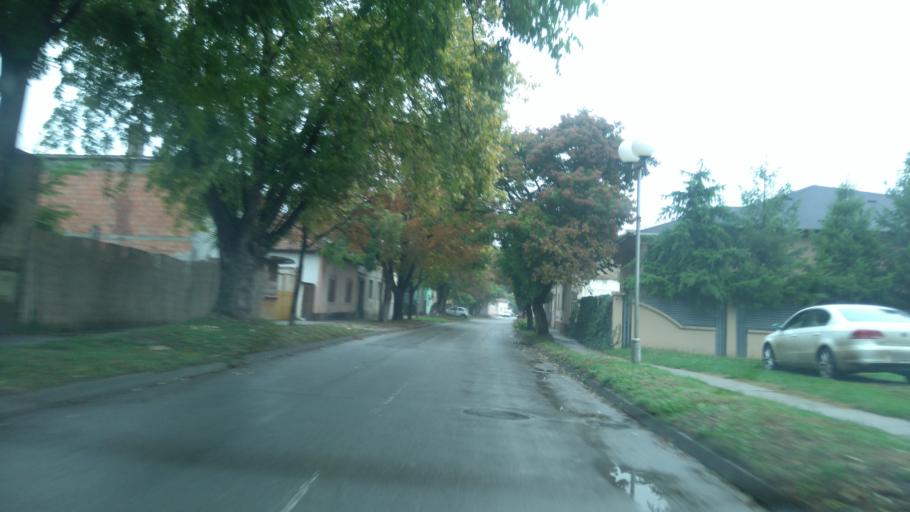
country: RS
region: Autonomna Pokrajina Vojvodina
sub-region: Juznobacki Okrug
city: Becej
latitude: 45.6149
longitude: 20.0521
